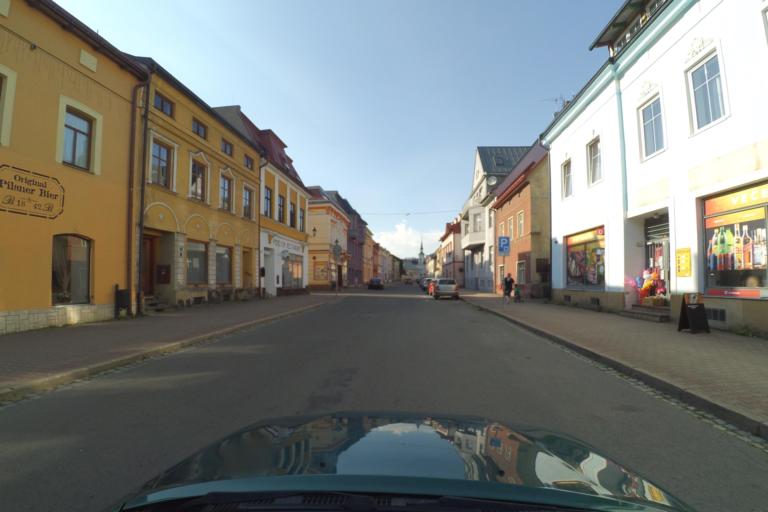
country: CZ
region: Kralovehradecky
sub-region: Okres Trutnov
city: Svoboda nad Upou
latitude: 50.6241
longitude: 15.8164
